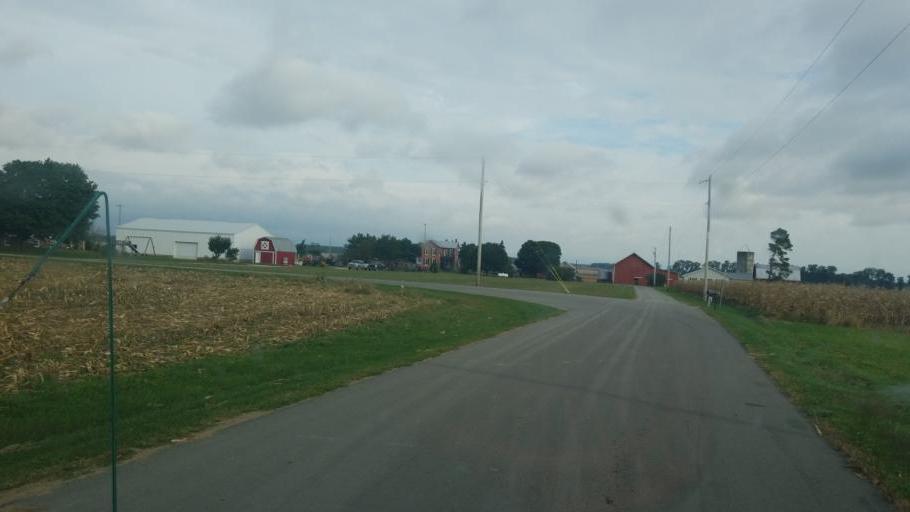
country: US
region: Ohio
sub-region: Wyandot County
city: Carey
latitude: 41.0111
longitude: -83.4399
